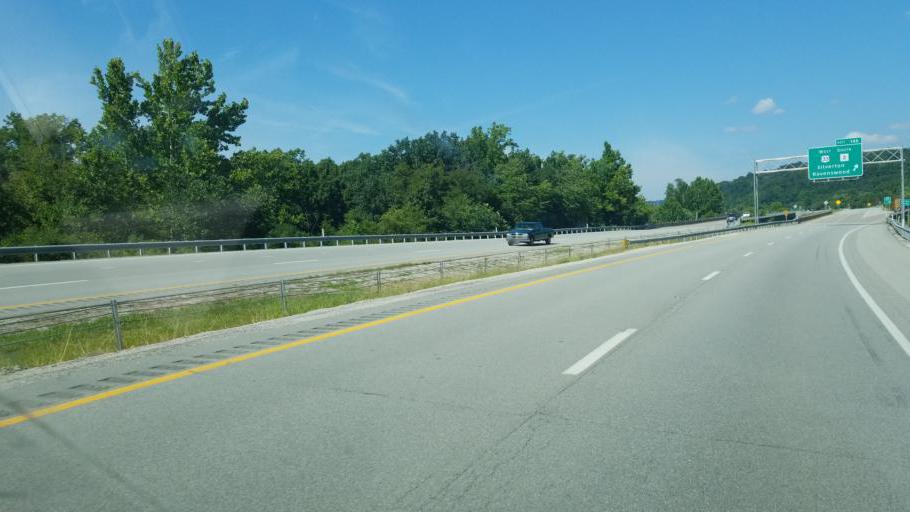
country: US
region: West Virginia
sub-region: Jackson County
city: Ravenswood
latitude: 38.9211
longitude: -81.7254
